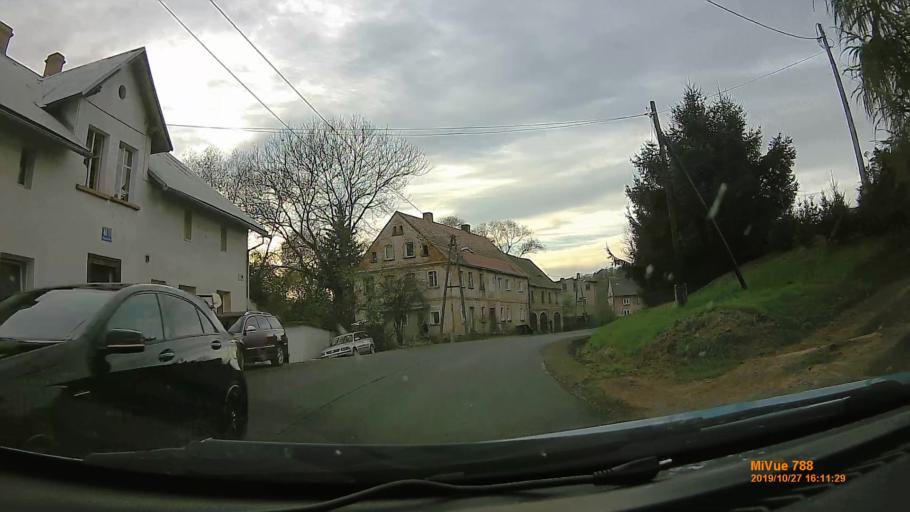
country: PL
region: Lower Silesian Voivodeship
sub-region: Powiat klodzki
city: Radkow
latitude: 50.5534
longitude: 16.4269
